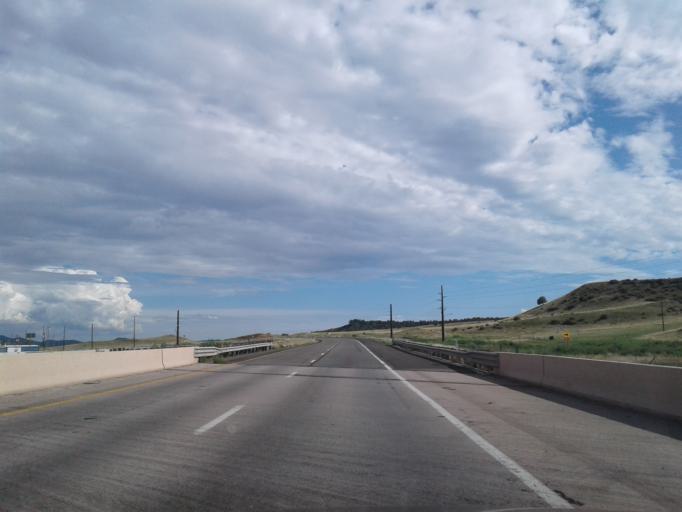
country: US
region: Arizona
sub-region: Yavapai County
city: Dewey-Humboldt
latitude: 34.5806
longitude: -112.2663
